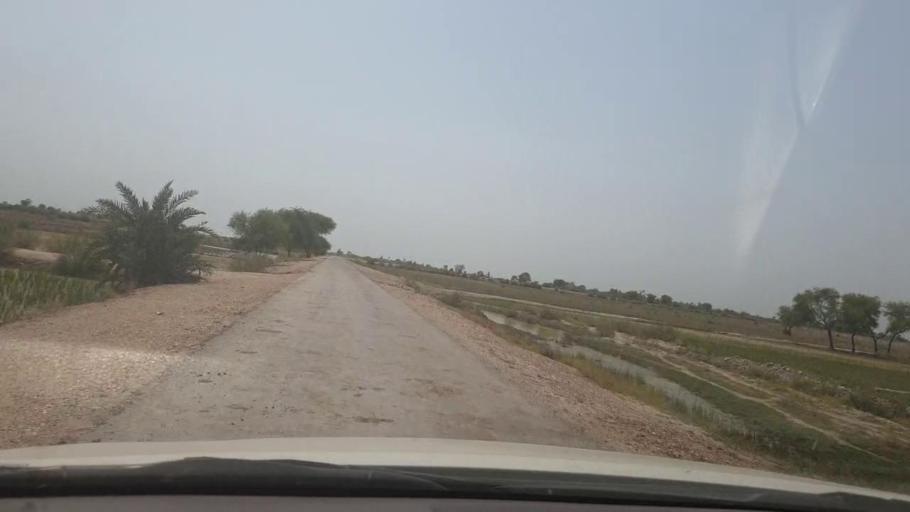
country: PK
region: Sindh
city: Shikarpur
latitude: 27.9931
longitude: 68.5548
